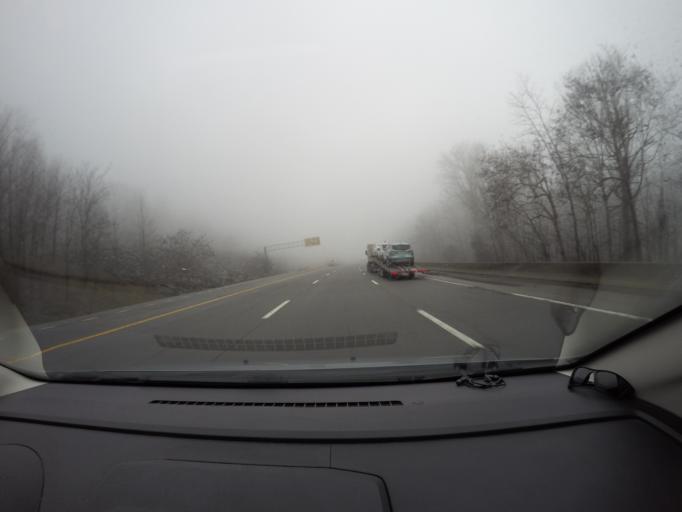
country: US
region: Tennessee
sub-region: Marion County
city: Monteagle
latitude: 35.1989
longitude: -85.8135
